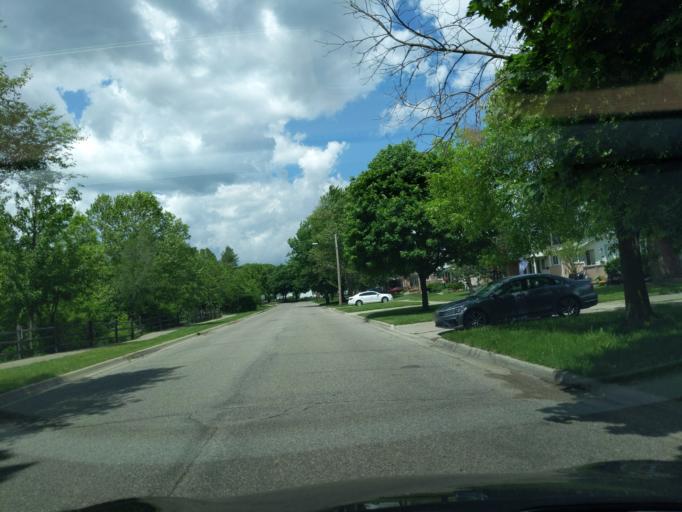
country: US
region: Michigan
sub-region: Ingham County
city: Lansing
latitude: 42.7468
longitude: -84.5211
